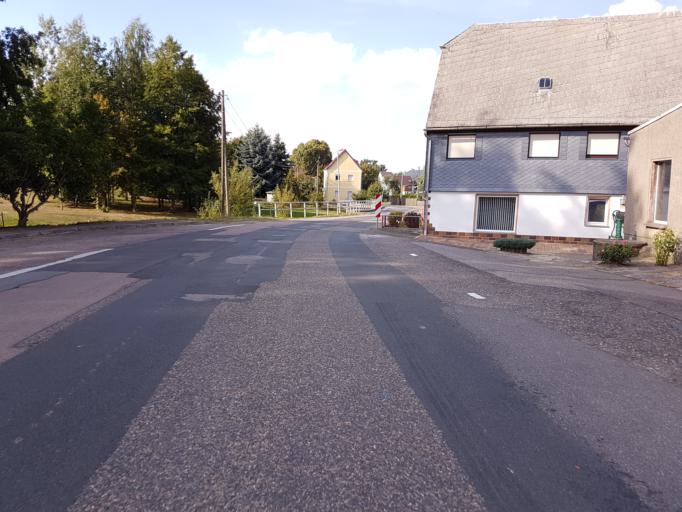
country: DE
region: Saxony
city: Claussnitz
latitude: 50.9684
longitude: 12.8849
